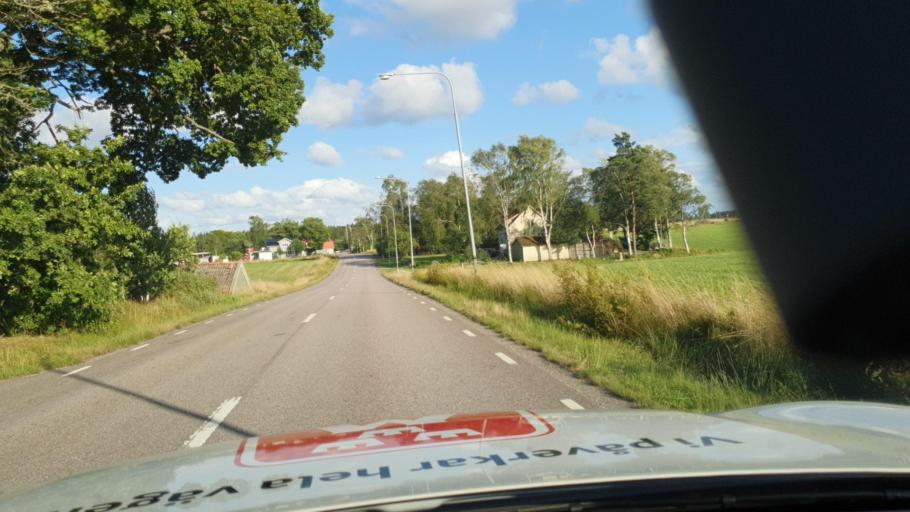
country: SE
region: Vaestra Goetaland
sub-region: Vanersborgs Kommun
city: Vanersborg
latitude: 58.4834
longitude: 12.2641
